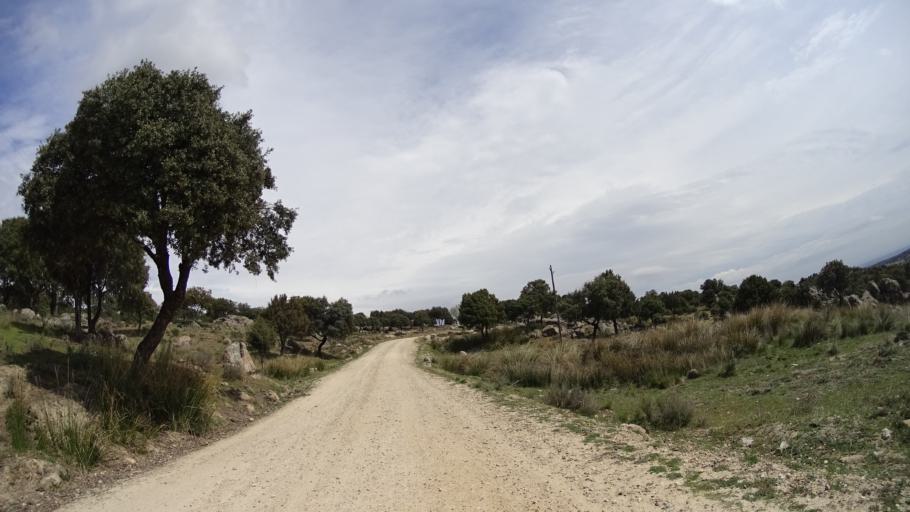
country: ES
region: Madrid
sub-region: Provincia de Madrid
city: Hoyo de Manzanares
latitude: 40.6206
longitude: -3.8836
